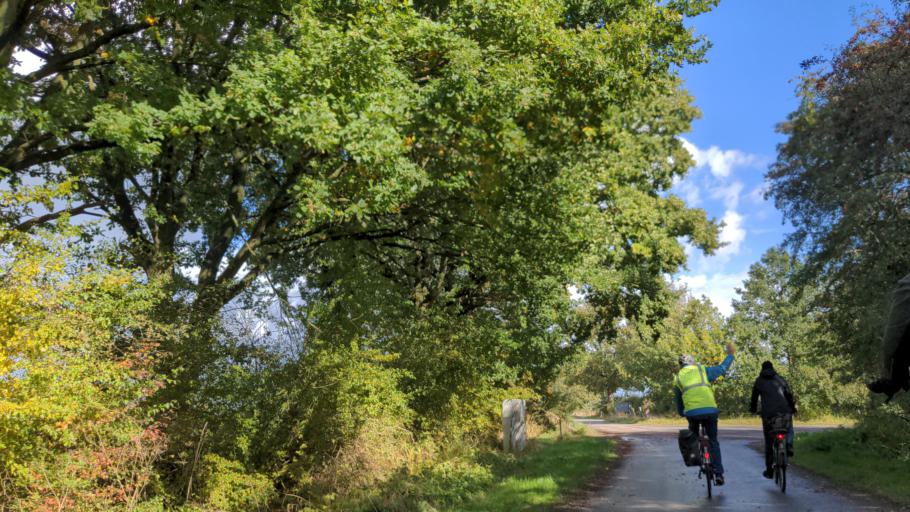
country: DE
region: Schleswig-Holstein
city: Klein Wesenberg
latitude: 53.8245
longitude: 10.5333
